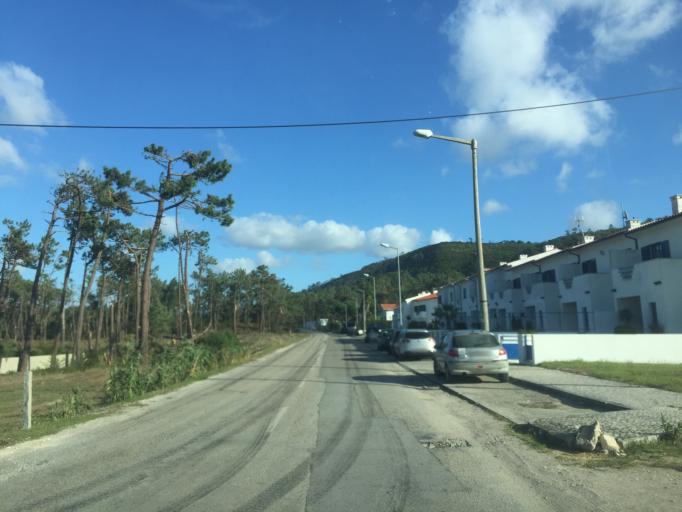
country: PT
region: Coimbra
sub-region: Figueira da Foz
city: Buarcos
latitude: 40.2156
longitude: -8.8884
